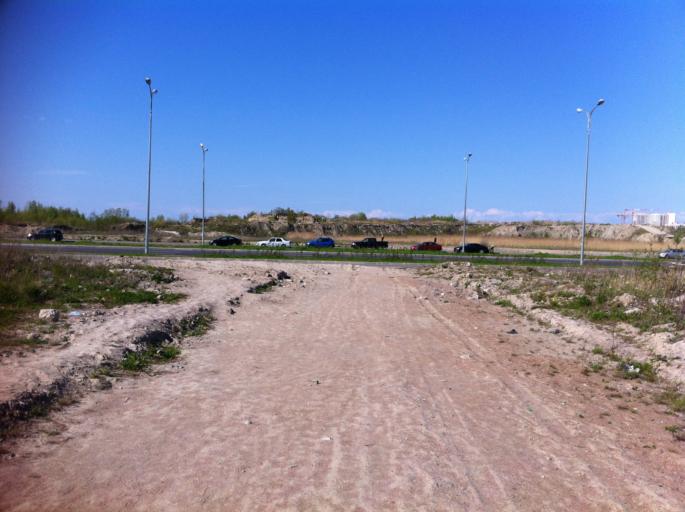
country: RU
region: St.-Petersburg
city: Sosnovaya Polyana
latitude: 59.8570
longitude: 30.1430
